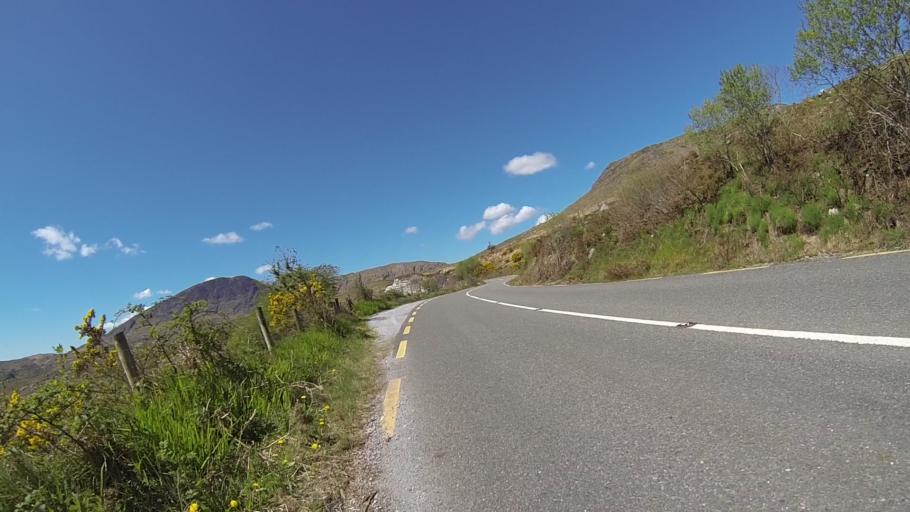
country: IE
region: Munster
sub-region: Ciarrai
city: Kenmare
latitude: 51.9259
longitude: -9.6353
